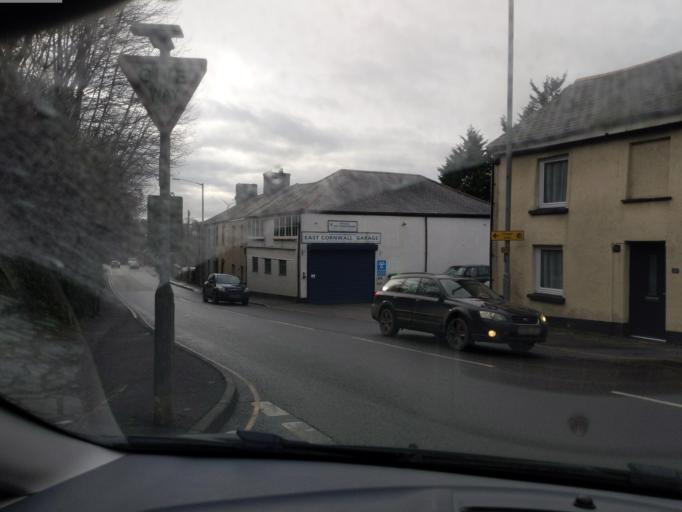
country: GB
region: England
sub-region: Cornwall
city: Launceston
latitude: 50.6350
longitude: -4.3639
